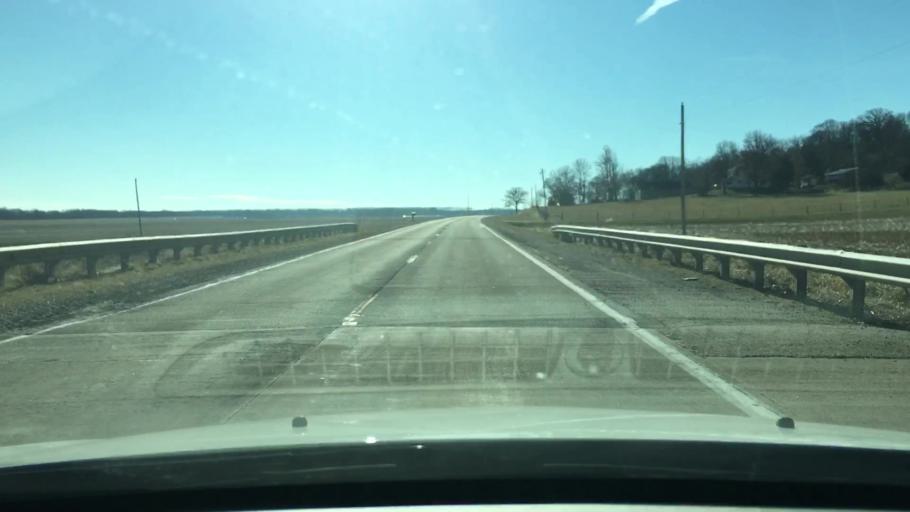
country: US
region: Illinois
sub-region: Mason County
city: Havana
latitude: 40.2619
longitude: -90.1778
